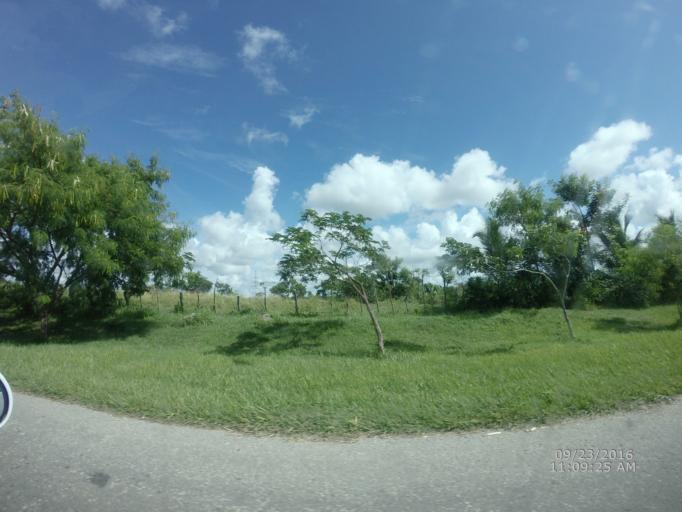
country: CU
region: La Habana
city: Arroyo Naranjo
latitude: 23.0181
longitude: -82.2444
